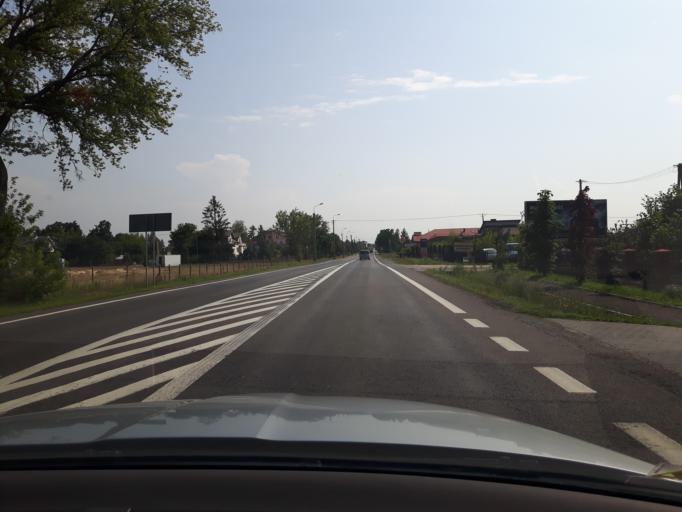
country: PL
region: Masovian Voivodeship
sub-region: Powiat mlawski
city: Strzegowo
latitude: 52.8987
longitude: 20.2862
